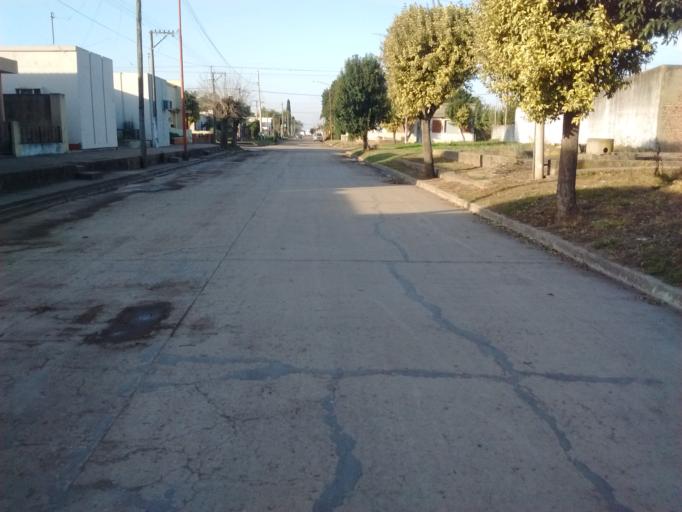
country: AR
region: Santa Fe
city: Galvez
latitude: -32.1669
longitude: -61.1592
